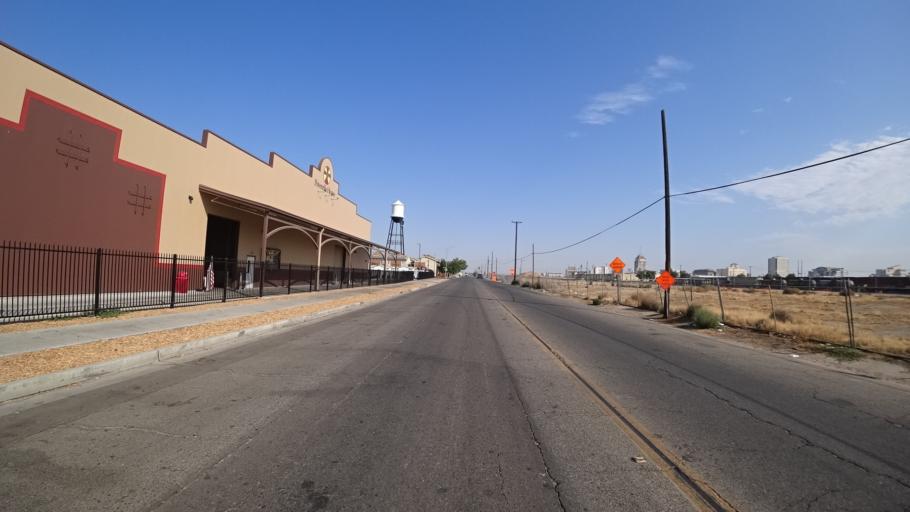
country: US
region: California
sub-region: Fresno County
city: Fresno
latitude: 36.7254
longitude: -119.7877
